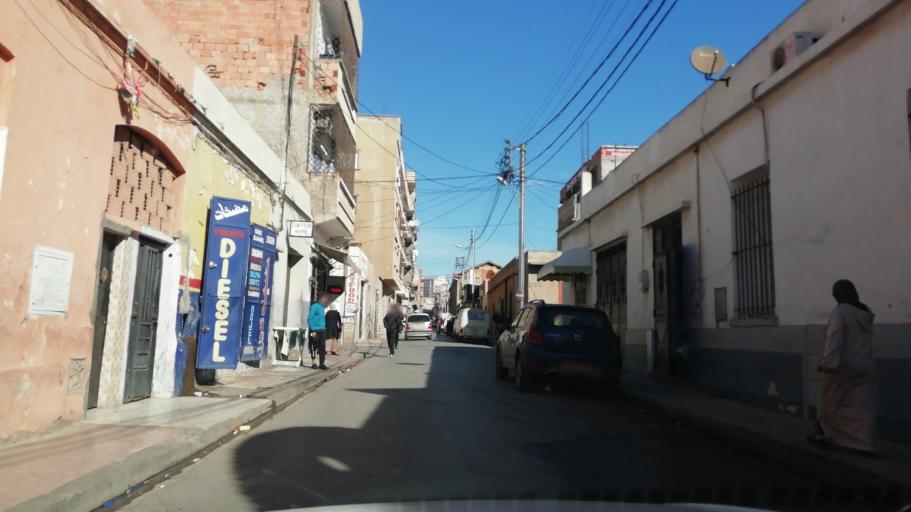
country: DZ
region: Oran
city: Oran
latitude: 35.6959
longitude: -0.6239
